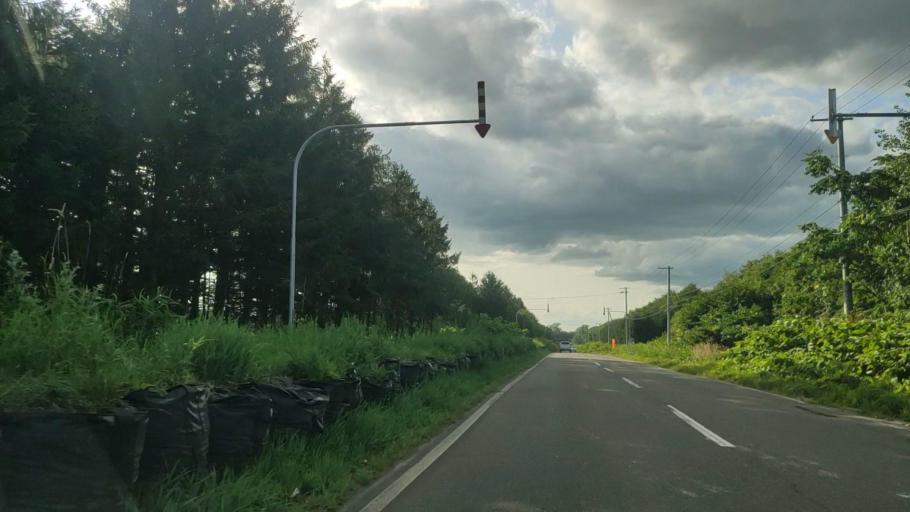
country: JP
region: Hokkaido
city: Makubetsu
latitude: 44.9009
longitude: 141.9110
